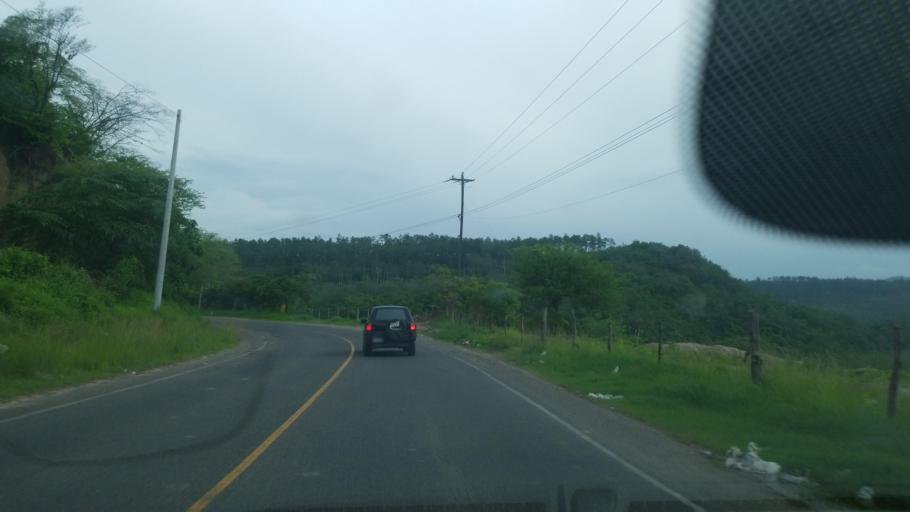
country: HN
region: Santa Barbara
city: Santa Barbara
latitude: 14.9157
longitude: -88.2523
